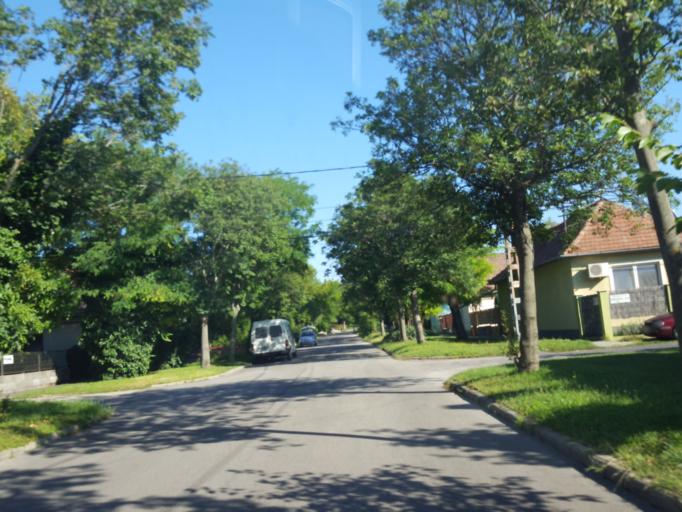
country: HU
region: Budapest
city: Budapest XXII. keruelet
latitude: 47.4208
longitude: 19.0201
